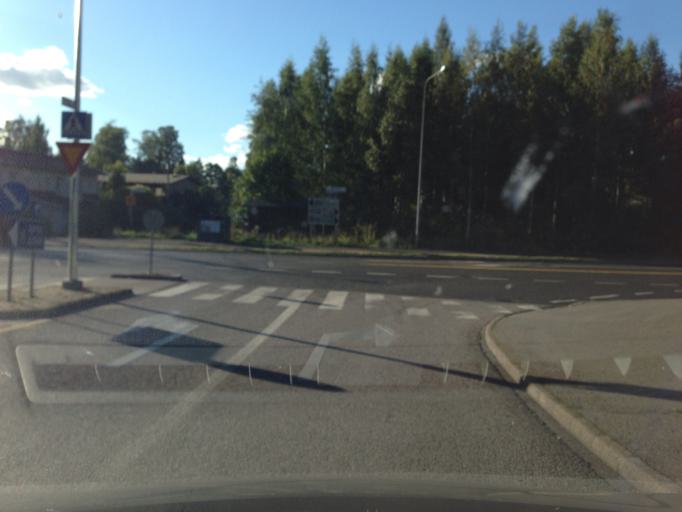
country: FI
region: Uusimaa
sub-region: Helsinki
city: Kerava
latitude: 60.3453
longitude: 25.0840
